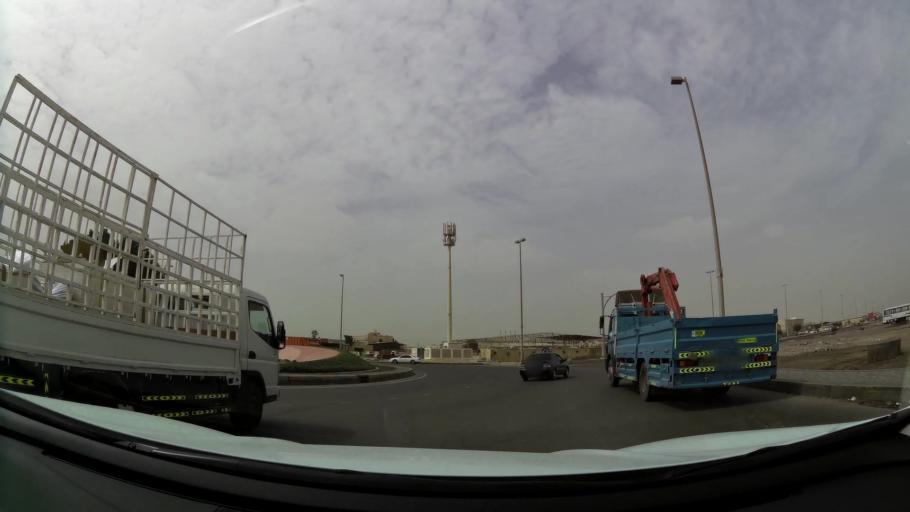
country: AE
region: Abu Dhabi
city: Abu Dhabi
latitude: 24.3553
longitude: 54.5123
